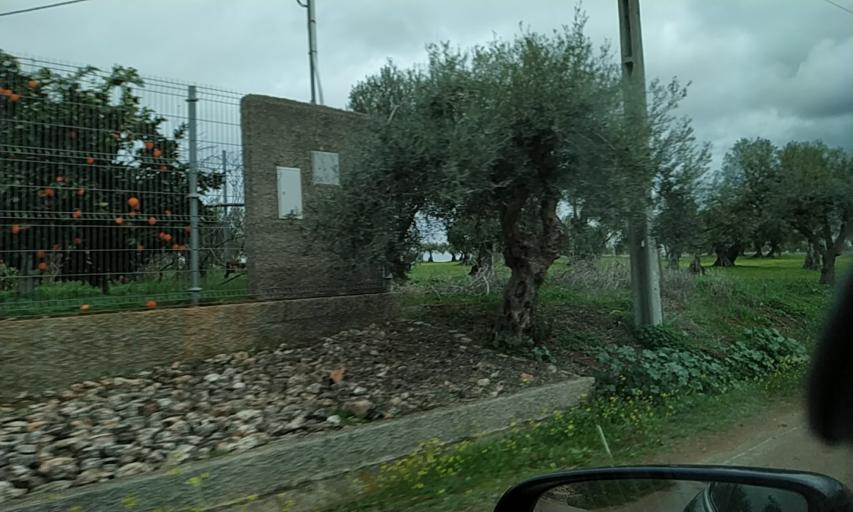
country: PT
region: Portalegre
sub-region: Campo Maior
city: Campo Maior
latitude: 39.0051
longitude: -7.0414
